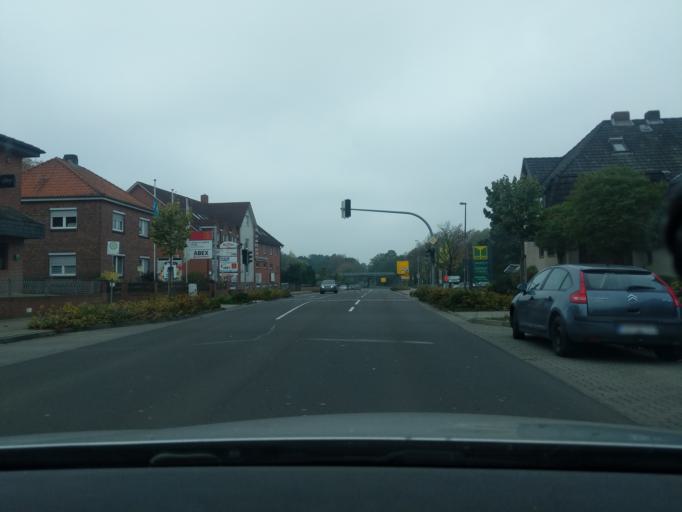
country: DE
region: Lower Saxony
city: Hemmoor
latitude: 53.6877
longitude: 9.1716
